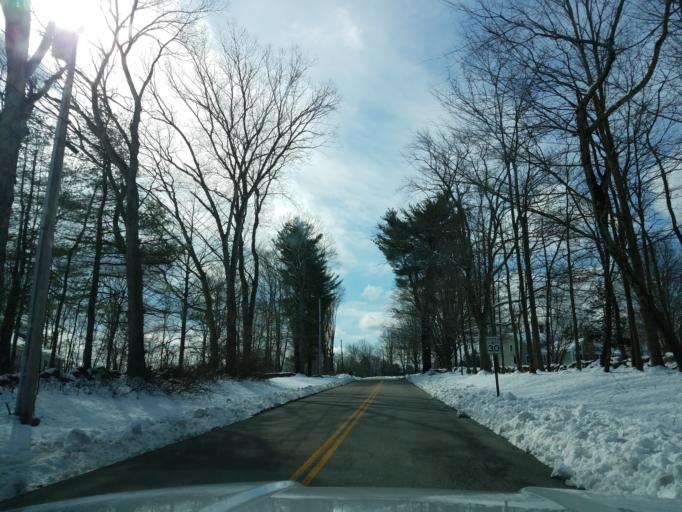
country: US
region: Connecticut
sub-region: New London County
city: Colchester
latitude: 41.5910
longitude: -72.3512
